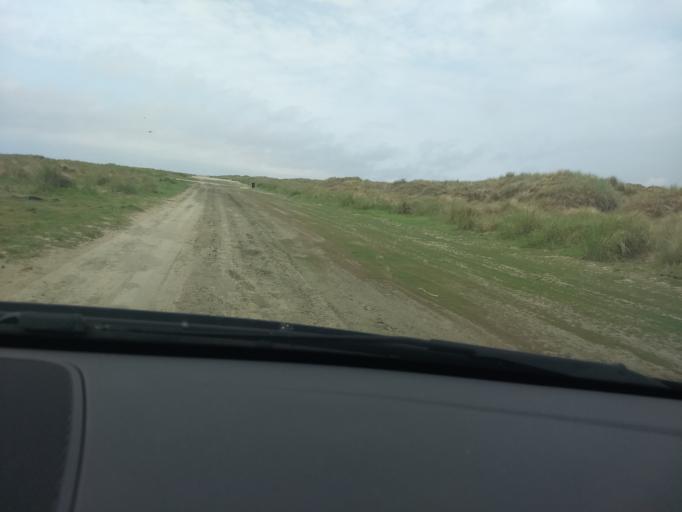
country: DK
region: South Denmark
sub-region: Fano Kommune
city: Nordby
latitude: 55.4088
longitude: 8.3861
